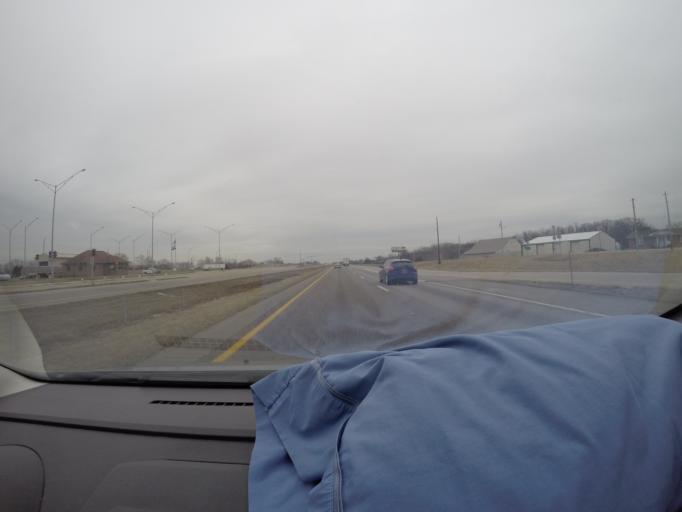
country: US
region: Missouri
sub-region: Saint Charles County
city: Wentzville
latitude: 38.8122
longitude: -90.9369
